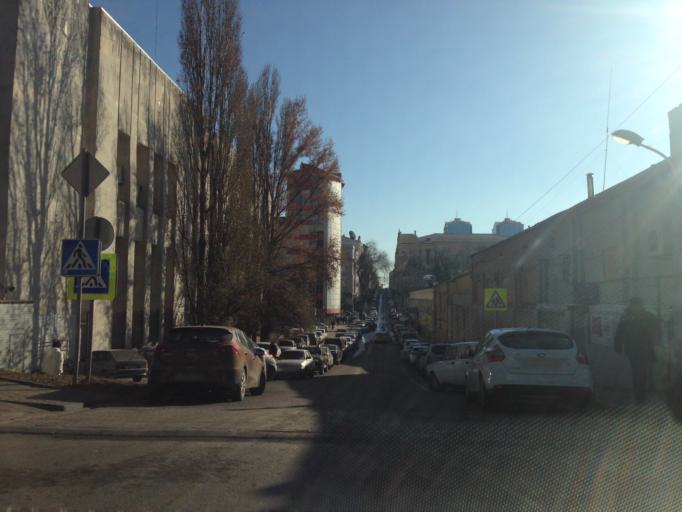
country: RU
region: Rostov
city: Rostov-na-Donu
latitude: 47.2244
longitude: 39.7118
